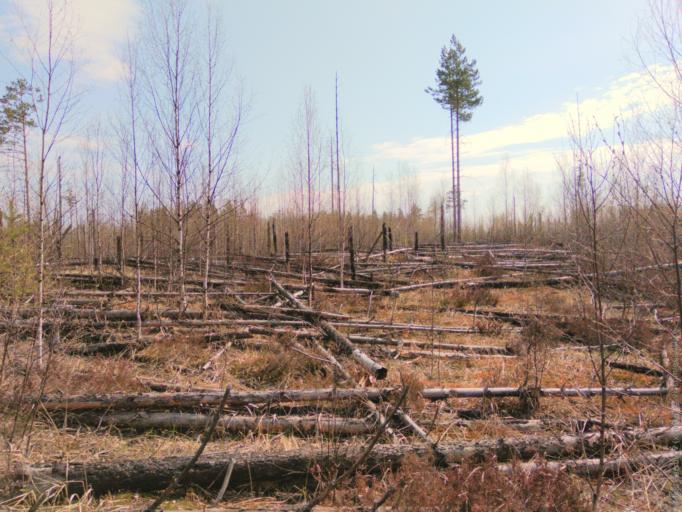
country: RU
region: Vladimir
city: Mezinovskiy
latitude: 55.5493
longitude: 40.3850
